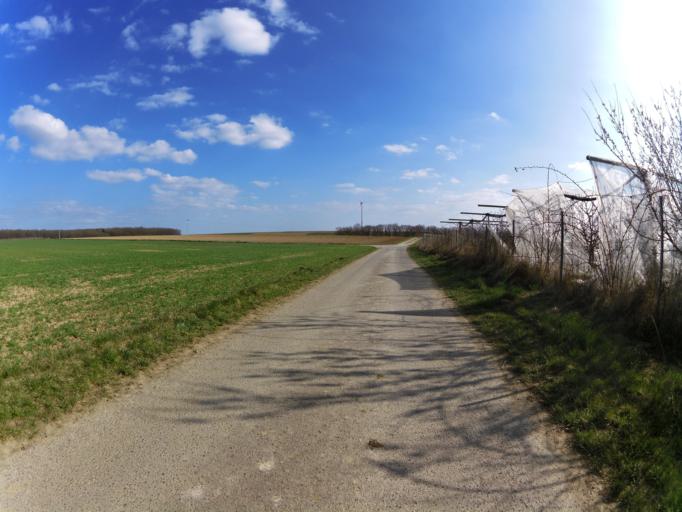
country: DE
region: Bavaria
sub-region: Regierungsbezirk Unterfranken
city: Prosselsheim
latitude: 49.8441
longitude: 10.1530
